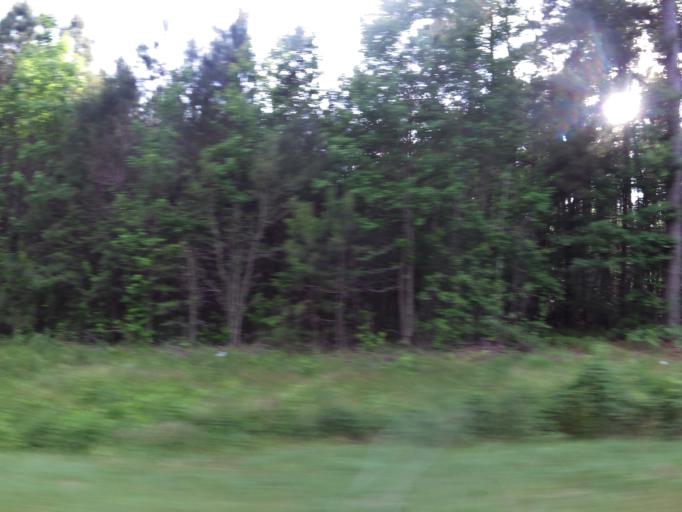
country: US
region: South Carolina
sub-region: Jasper County
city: Ridgeland
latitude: 32.5165
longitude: -81.1454
